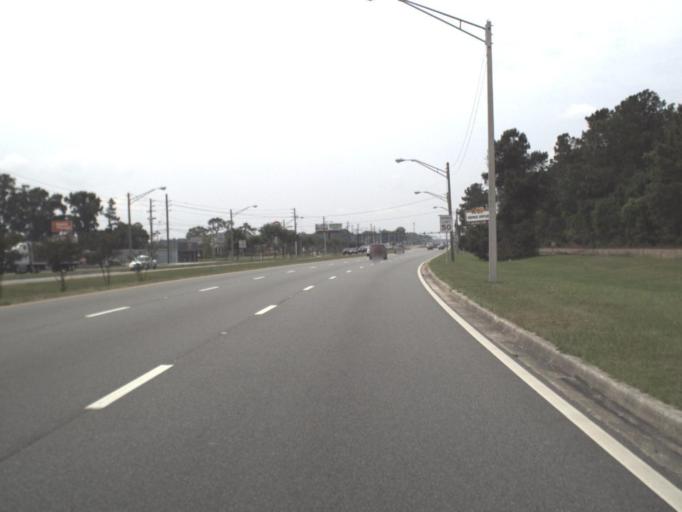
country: US
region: Florida
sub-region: Clay County
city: Orange Park
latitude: 30.2395
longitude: -81.6967
